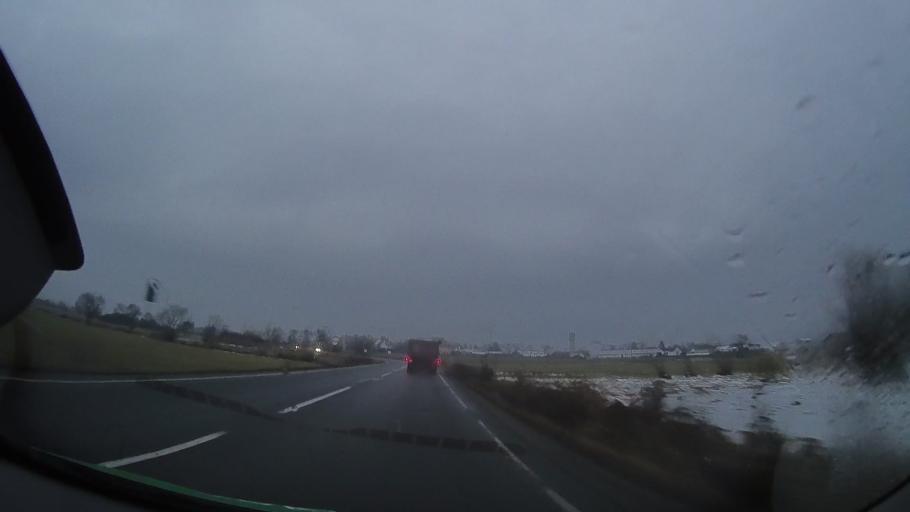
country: RO
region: Harghita
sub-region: Comuna Lazarea
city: Lazarea
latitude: 46.7627
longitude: 25.5149
